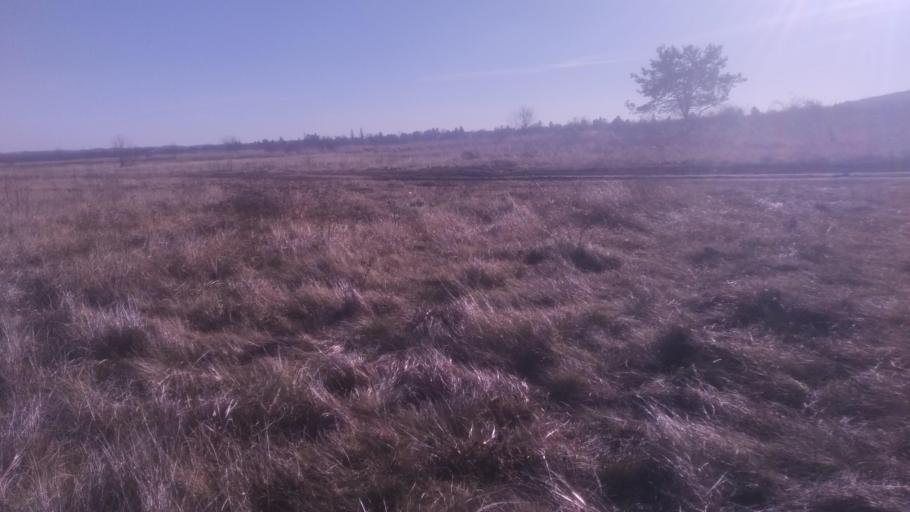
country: HU
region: Pest
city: Budakalasz
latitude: 47.6393
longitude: 19.0503
